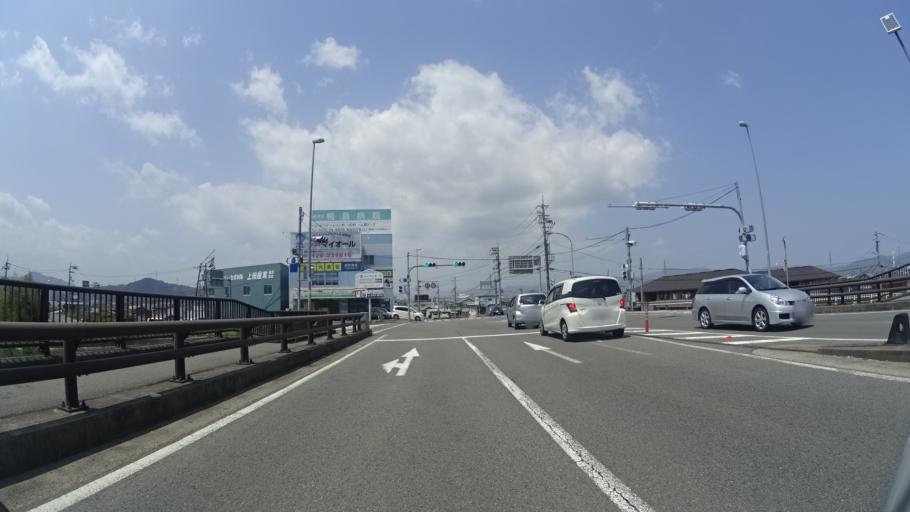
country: JP
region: Tokushima
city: Ishii
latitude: 34.0731
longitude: 134.4970
